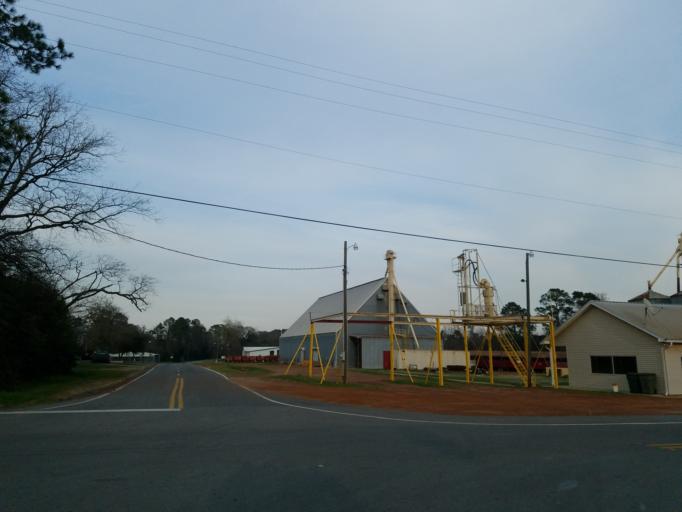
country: US
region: Georgia
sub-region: Tift County
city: Omega
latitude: 31.3401
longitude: -83.5933
